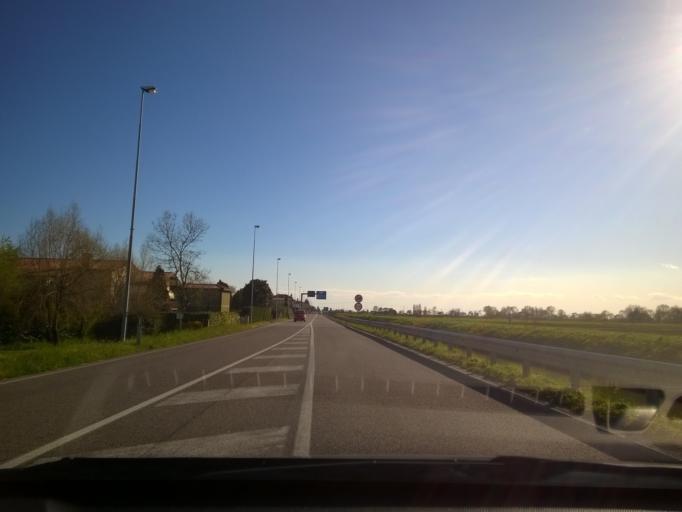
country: IT
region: Veneto
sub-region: Provincia di Venezia
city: Fossalta di Piave
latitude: 45.6182
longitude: 12.4952
